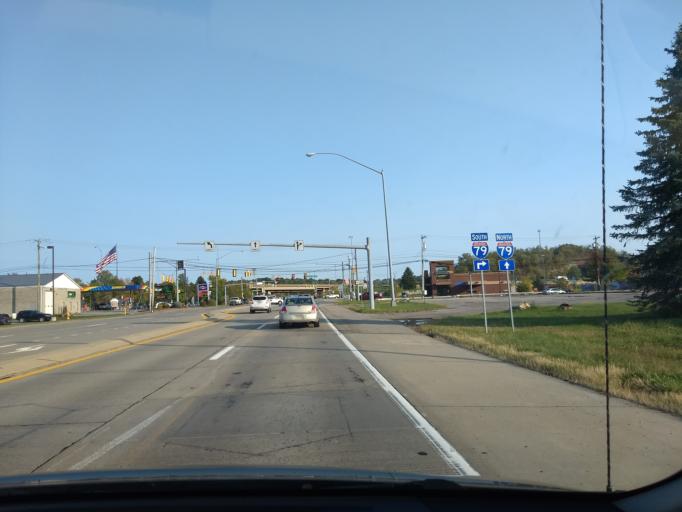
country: US
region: Pennsylvania
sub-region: Allegheny County
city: Bridgeville
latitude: 40.3575
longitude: -80.1215
